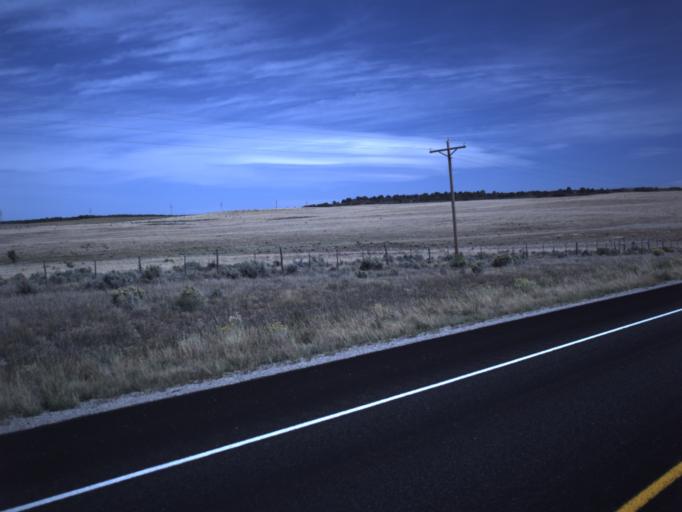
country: US
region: Utah
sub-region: San Juan County
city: Monticello
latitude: 37.8681
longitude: -109.2426
